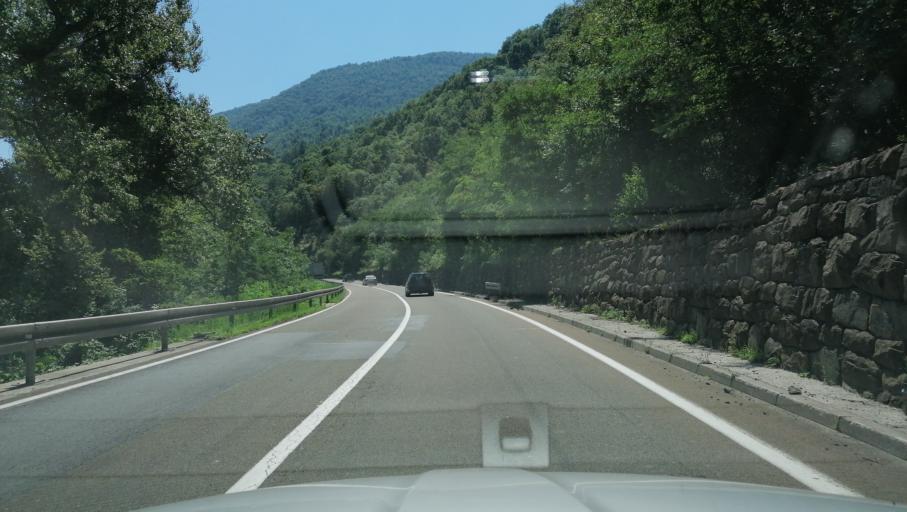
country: RS
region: Central Serbia
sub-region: Raski Okrug
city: Kraljevo
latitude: 43.5785
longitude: 20.5865
